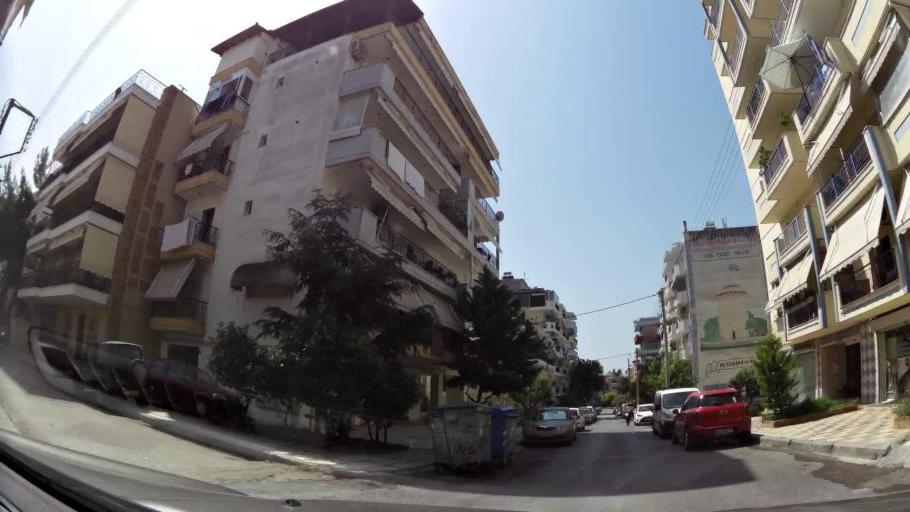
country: GR
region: Central Macedonia
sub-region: Nomos Thessalonikis
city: Evosmos
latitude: 40.6738
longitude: 22.9144
